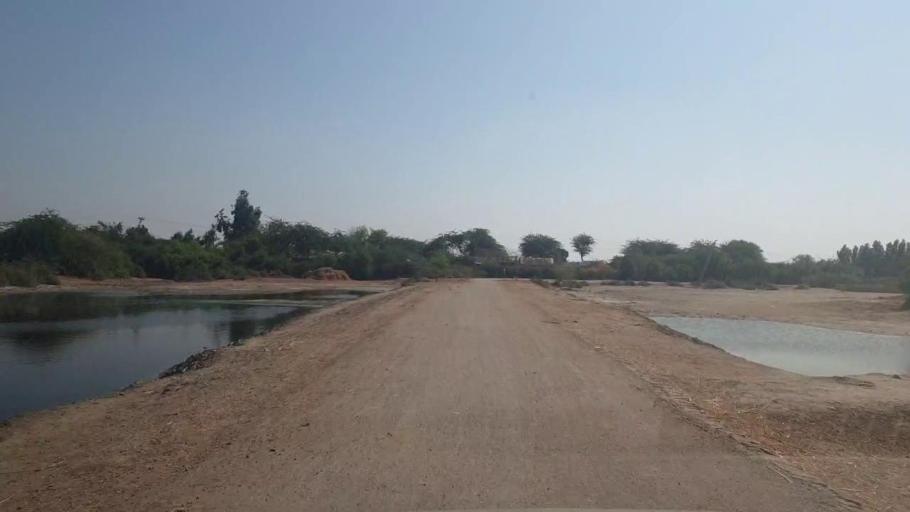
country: PK
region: Sindh
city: Badin
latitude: 24.6392
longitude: 68.9136
